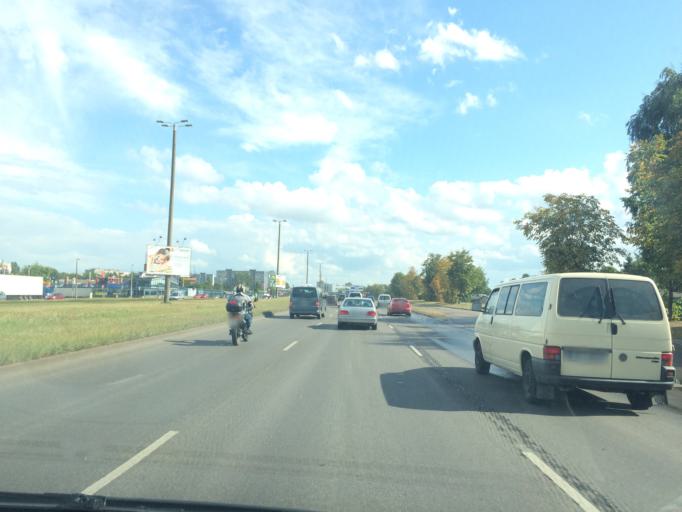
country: LV
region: Riga
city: Riga
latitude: 56.9286
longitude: 24.1549
